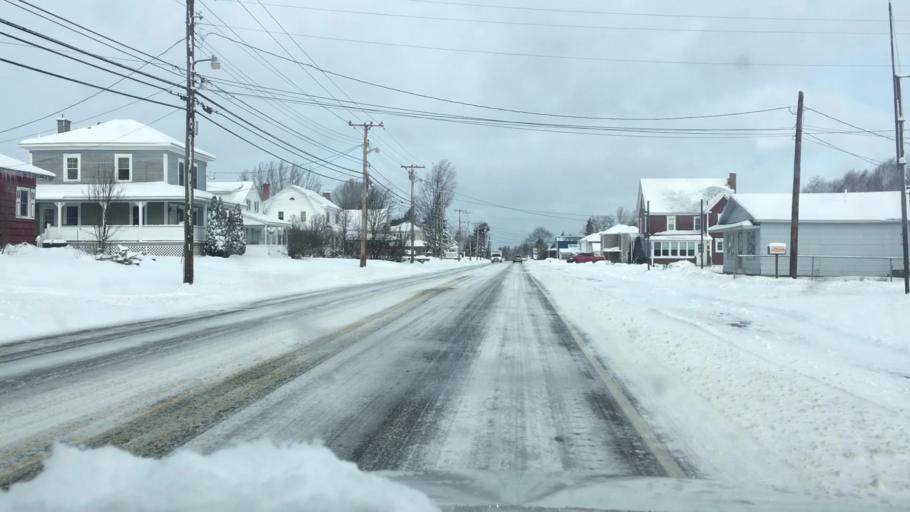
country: US
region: Maine
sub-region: Aroostook County
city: Van Buren
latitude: 47.1658
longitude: -67.9424
